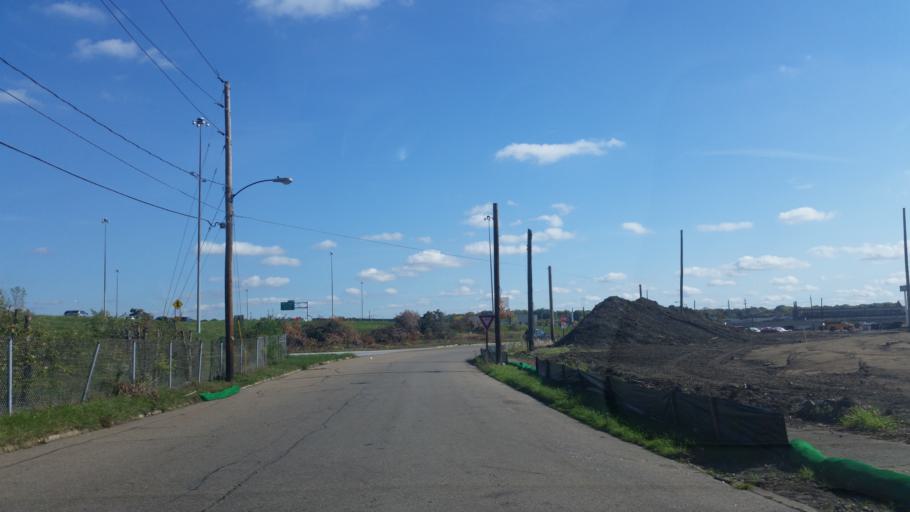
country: US
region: Ohio
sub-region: Summit County
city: Akron
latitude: 41.0617
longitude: -81.5302
